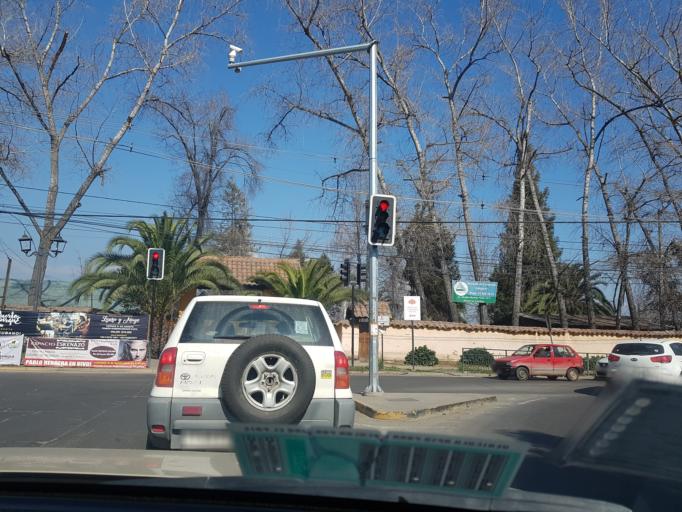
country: CL
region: Santiago Metropolitan
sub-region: Provincia de Cordillera
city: Puente Alto
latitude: -33.6354
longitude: -70.5731
